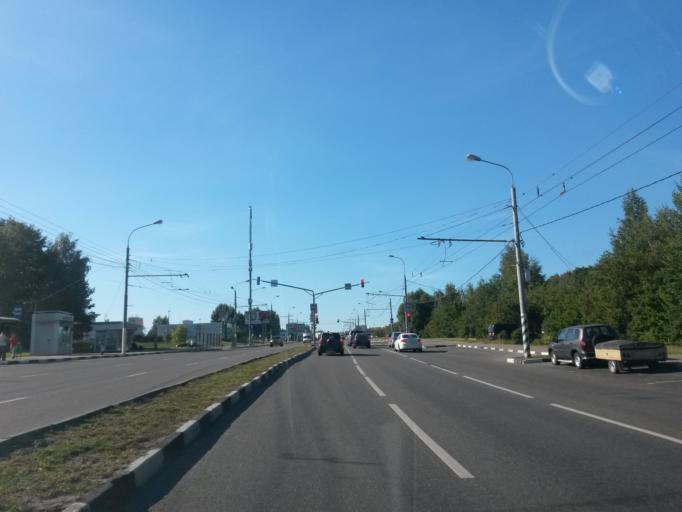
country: RU
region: Moscow
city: Yasenevo
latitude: 55.6095
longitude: 37.5210
